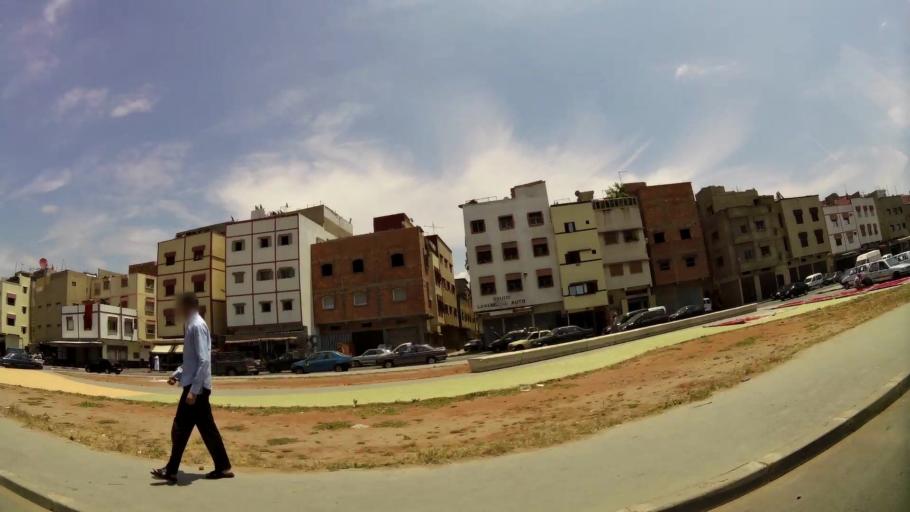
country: MA
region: Rabat-Sale-Zemmour-Zaer
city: Sale
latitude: 34.0686
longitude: -6.7781
